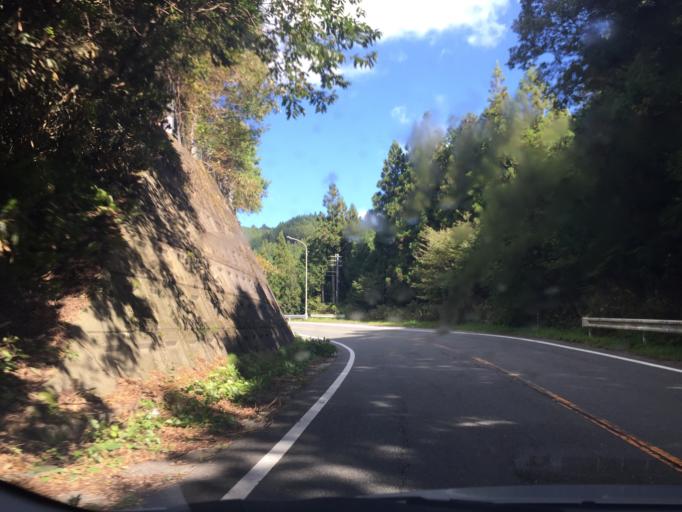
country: JP
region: Nagano
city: Iida
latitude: 35.2207
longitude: 137.6926
